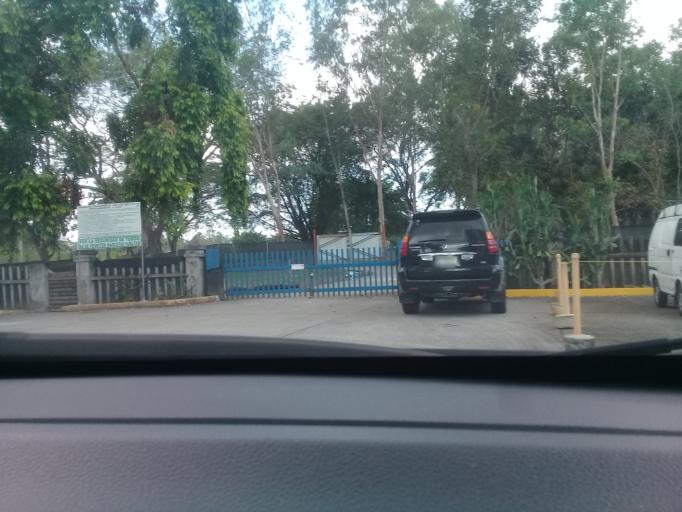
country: PA
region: Panama
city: San Miguelito
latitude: 9.0118
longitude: -79.4702
